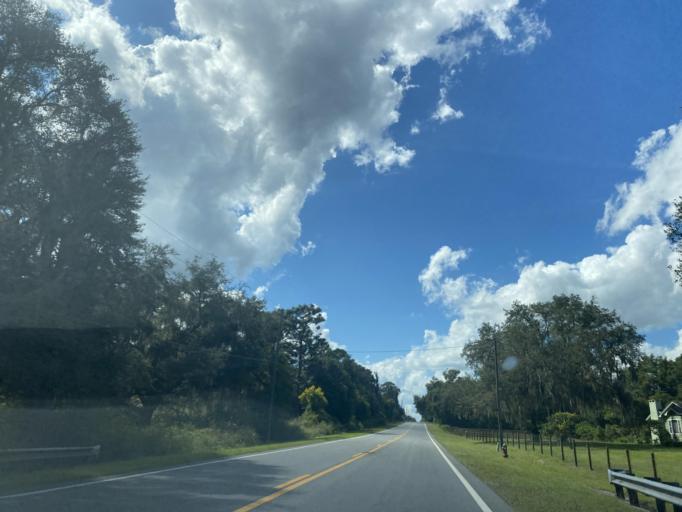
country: US
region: Florida
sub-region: Sumter County
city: The Villages
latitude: 28.9820
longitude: -81.9558
